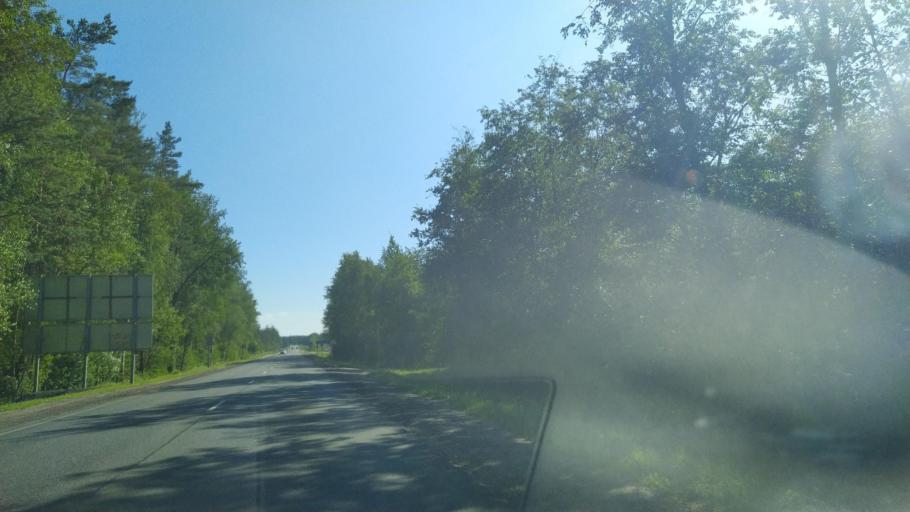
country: RU
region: Leningrad
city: Kirovsk
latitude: 59.9176
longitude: 30.9399
